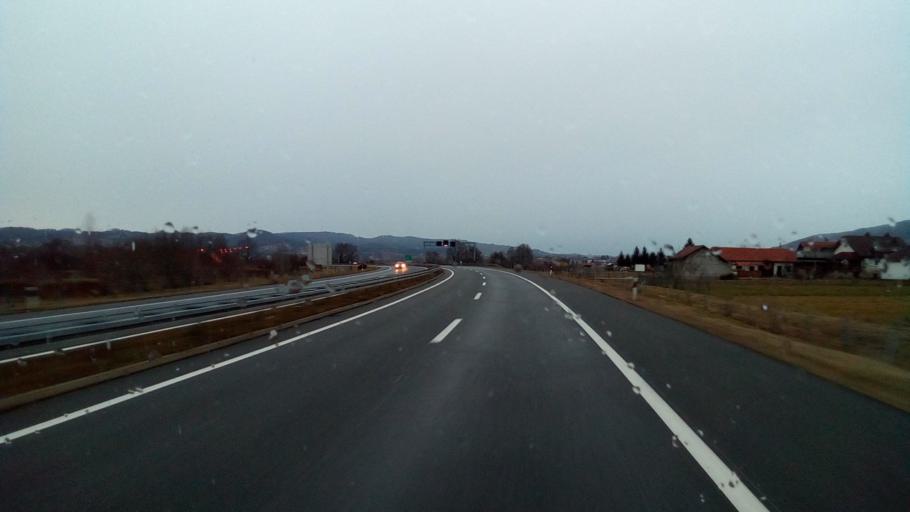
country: HR
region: Varazdinska
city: Ljubescica
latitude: 46.1575
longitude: 16.3740
